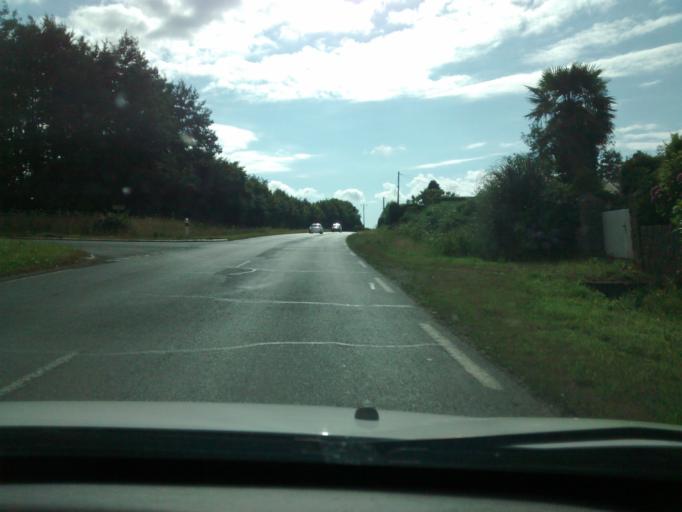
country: FR
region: Brittany
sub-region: Departement des Cotes-d'Armor
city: Rospez
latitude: 48.7459
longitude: -3.3673
